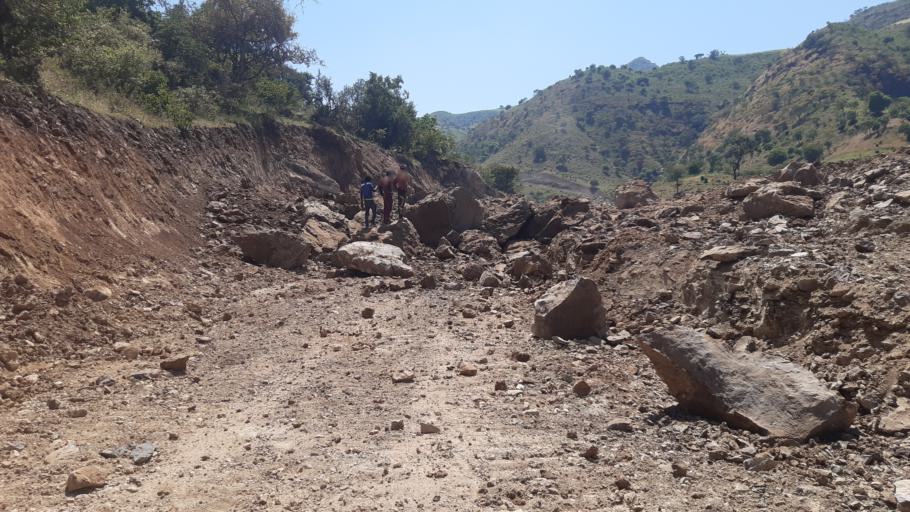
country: ET
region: Amhara
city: Dabat
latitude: 13.1776
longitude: 37.5975
